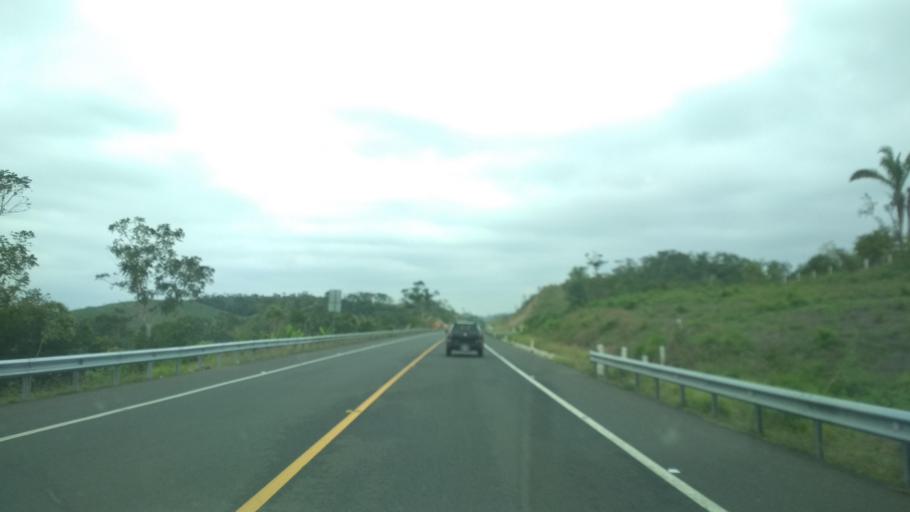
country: MX
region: Veracruz
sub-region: Papantla
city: Polutla
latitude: 20.4467
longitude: -97.2395
